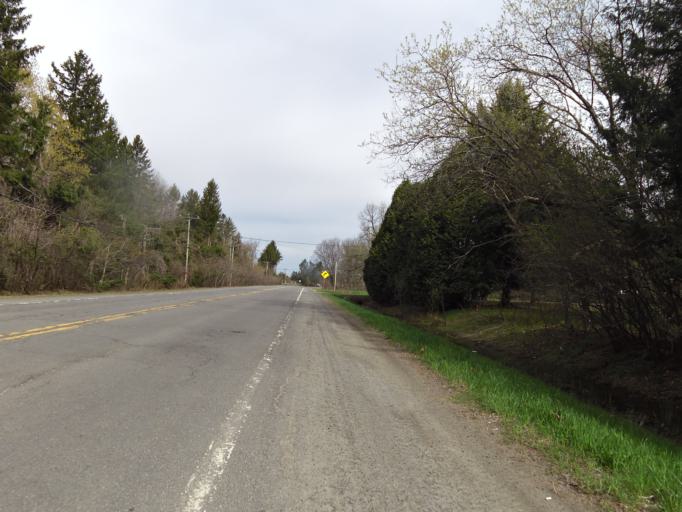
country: CA
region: Quebec
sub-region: Monteregie
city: Hudson
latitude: 45.4743
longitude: -74.1259
